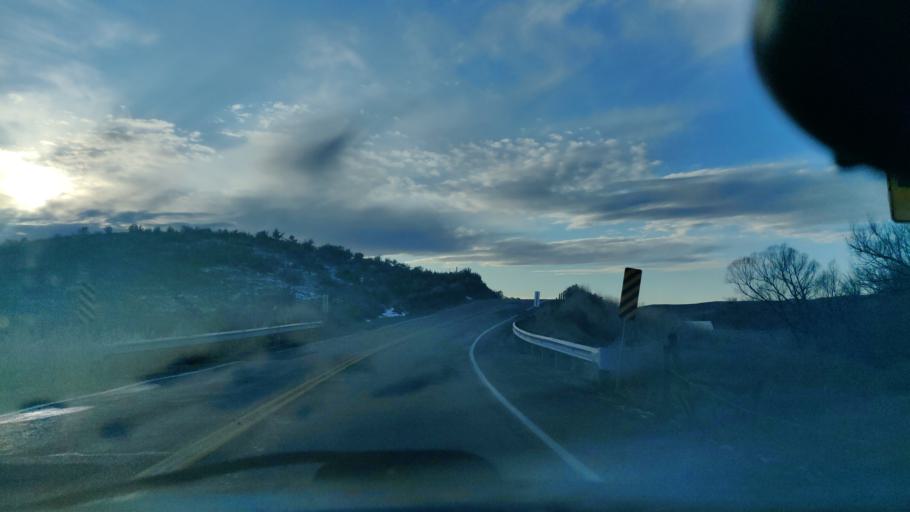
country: US
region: Idaho
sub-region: Ada County
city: Eagle
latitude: 43.7303
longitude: -116.2862
